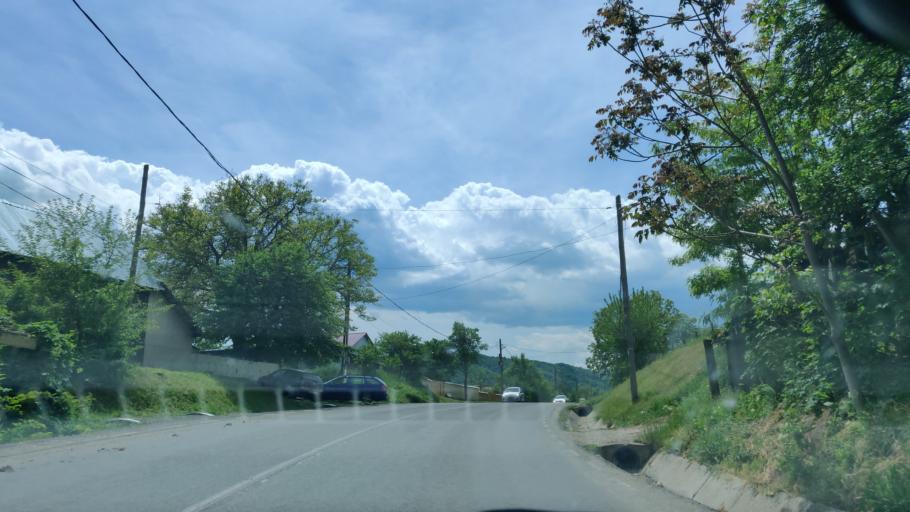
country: RO
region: Vrancea
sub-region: Comuna Vidra
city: Vidra
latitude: 45.9035
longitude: 26.8921
